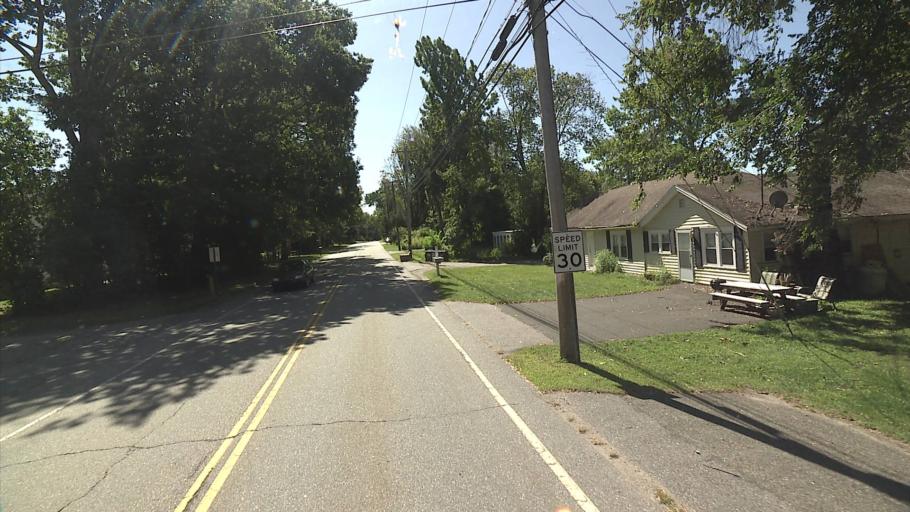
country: US
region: Connecticut
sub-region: Litchfield County
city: Litchfield
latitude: 41.7052
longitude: -73.2341
